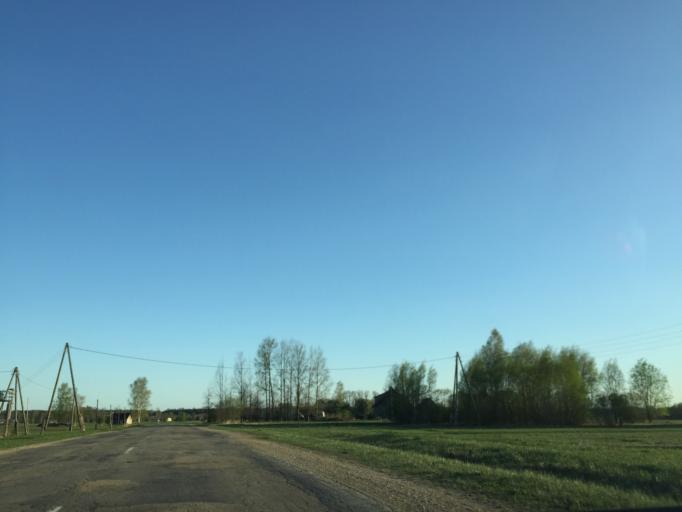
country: LV
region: Koknese
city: Koknese
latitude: 56.6863
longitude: 25.4869
